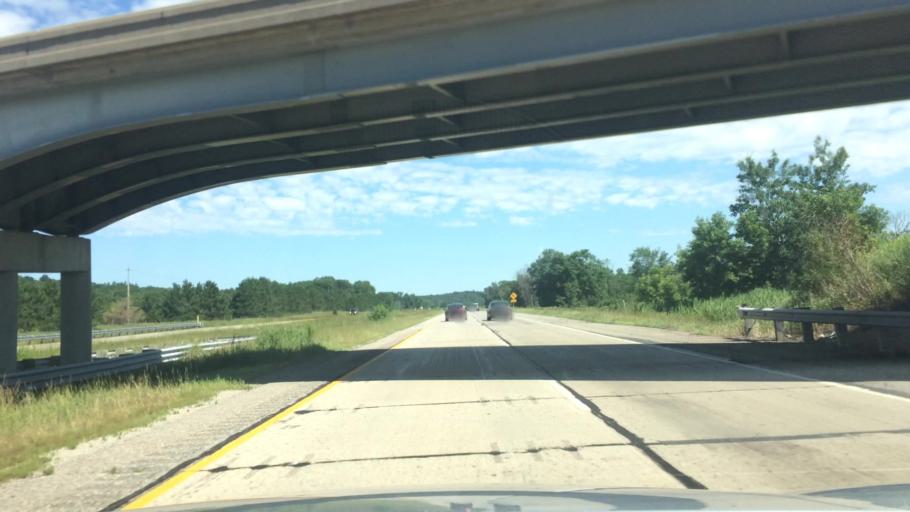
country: US
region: Wisconsin
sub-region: Marquette County
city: Westfield
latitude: 43.7592
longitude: -89.4841
